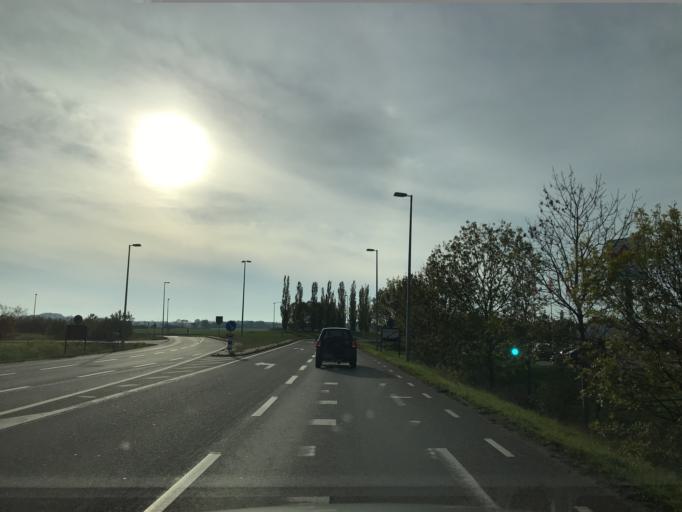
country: SE
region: Skane
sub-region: Helsingborg
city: Hyllinge
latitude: 56.0997
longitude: 12.8537
